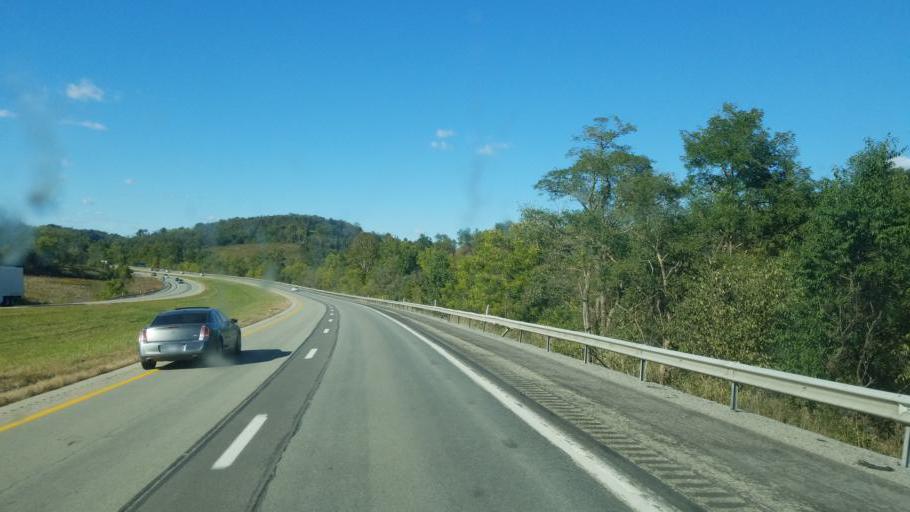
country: US
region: Pennsylvania
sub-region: Washington County
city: East Washington
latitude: 40.0960
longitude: -80.1930
